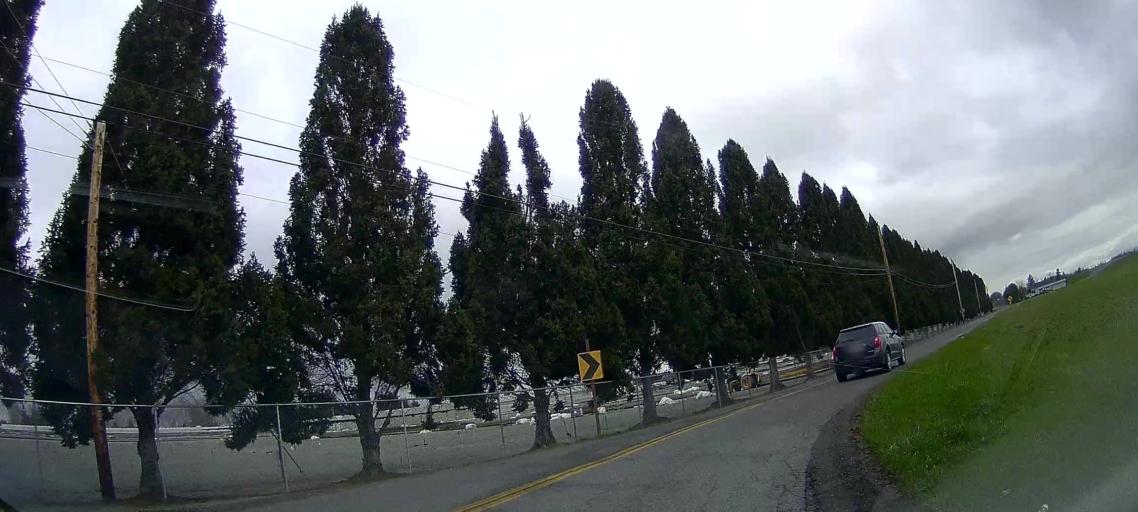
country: US
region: Washington
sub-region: Skagit County
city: Mount Vernon
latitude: 48.4433
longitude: -122.3573
